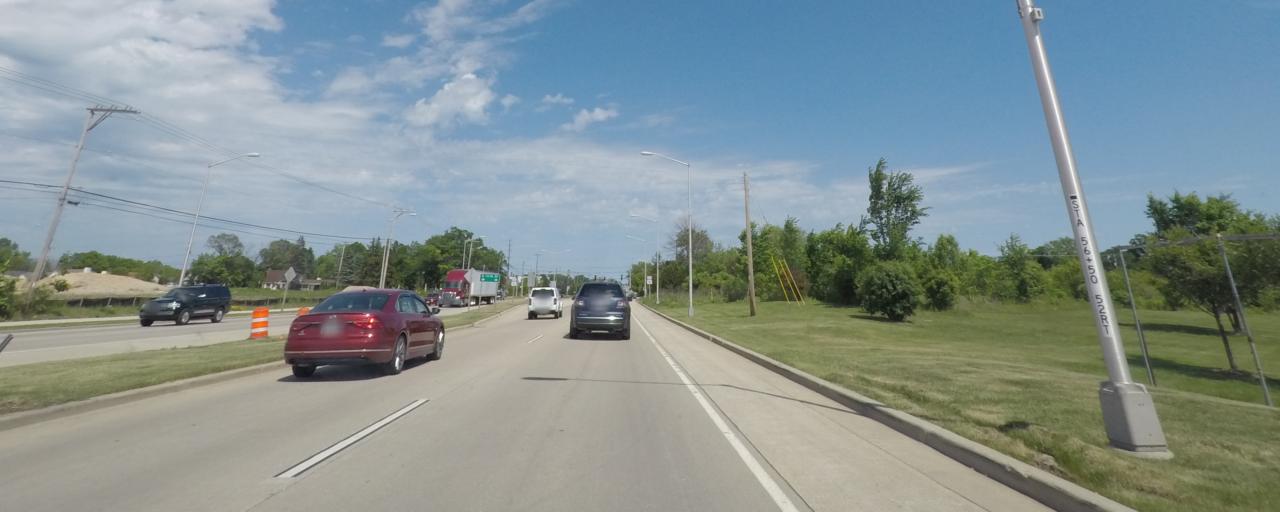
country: US
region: Wisconsin
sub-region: Milwaukee County
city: Oak Creek
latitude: 42.9016
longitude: -87.9339
